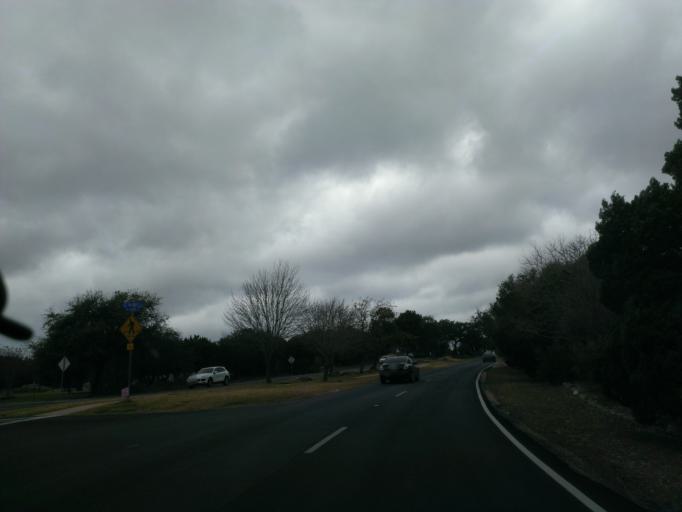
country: US
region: Texas
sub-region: Travis County
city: The Hills
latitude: 30.3516
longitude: -97.9938
